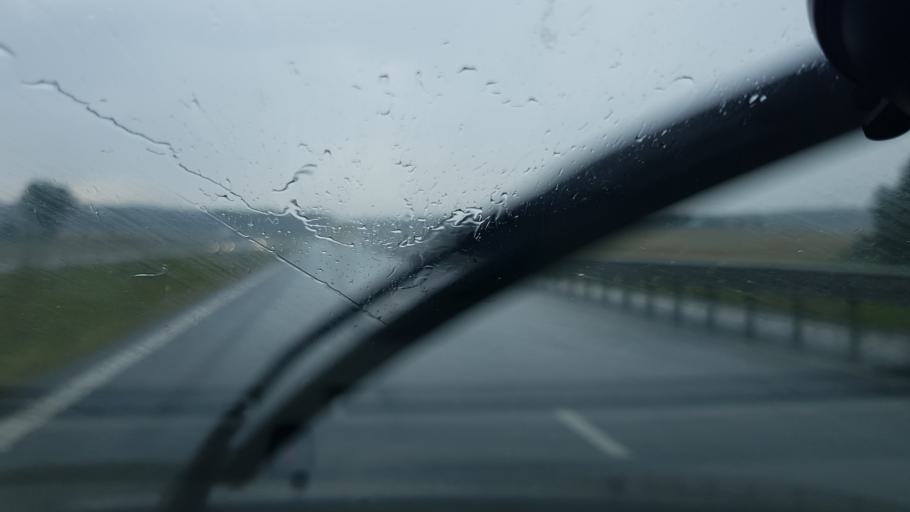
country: PL
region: Warmian-Masurian Voivodeship
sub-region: Powiat nidzicki
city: Nidzica
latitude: 53.4464
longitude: 20.3306
